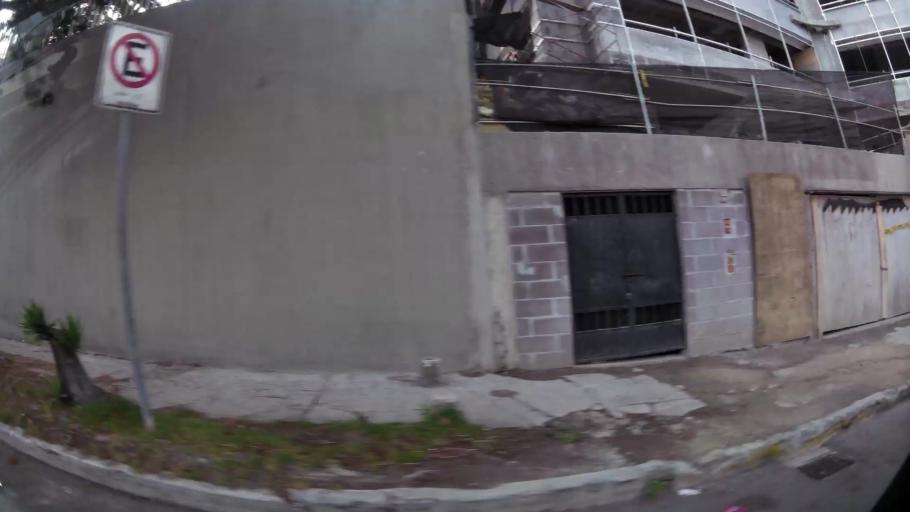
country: EC
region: Pichincha
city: Quito
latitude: -0.2011
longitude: -78.4814
